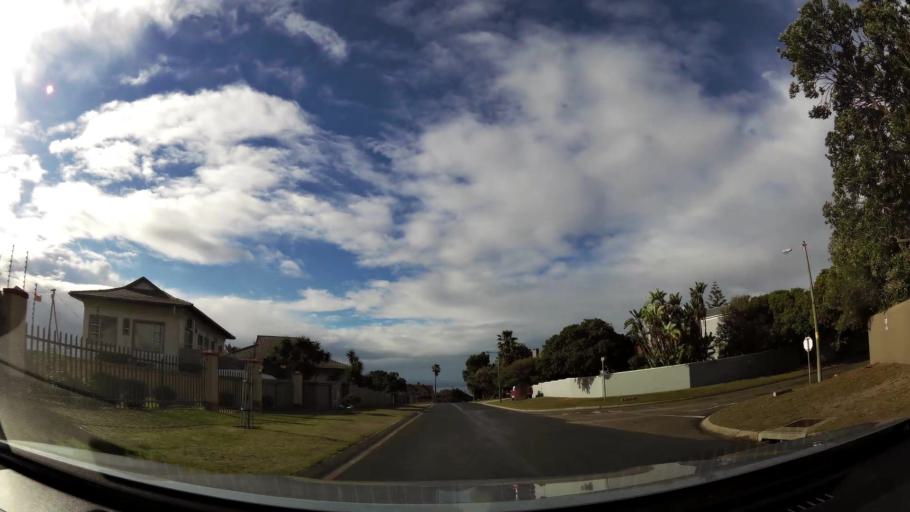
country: ZA
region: Western Cape
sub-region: Eden District Municipality
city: Mossel Bay
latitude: -34.1910
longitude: 22.1379
